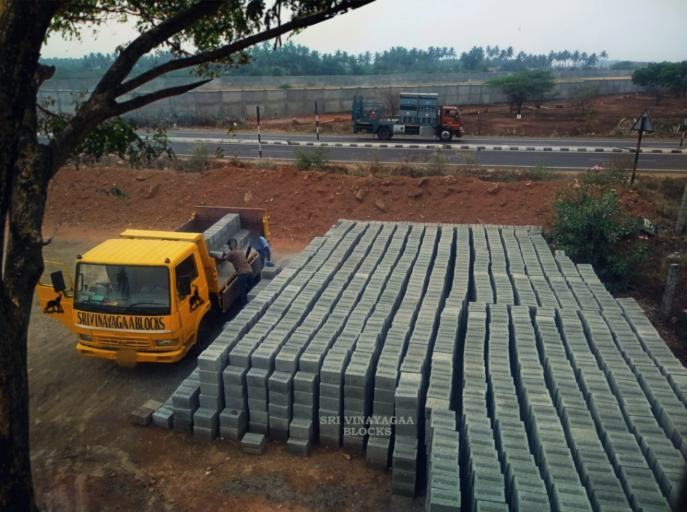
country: IN
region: Tamil Nadu
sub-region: Coimbatore
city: Sulur
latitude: 11.0248
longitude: 77.1721
